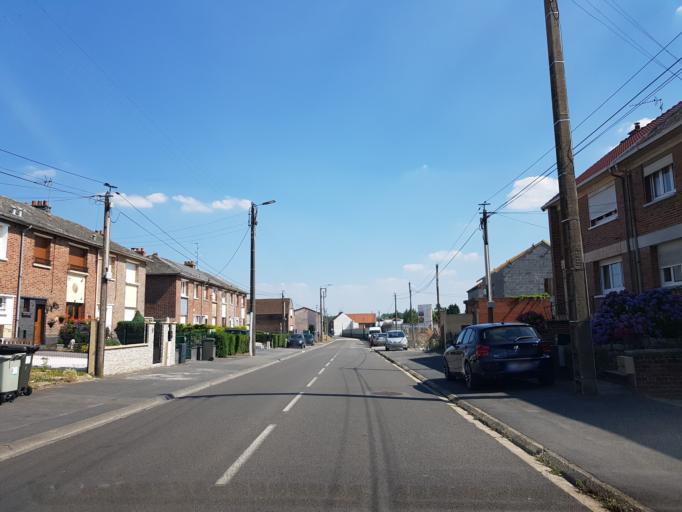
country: FR
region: Nord-Pas-de-Calais
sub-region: Departement du Nord
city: Roeulx
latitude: 50.3134
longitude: 3.3325
